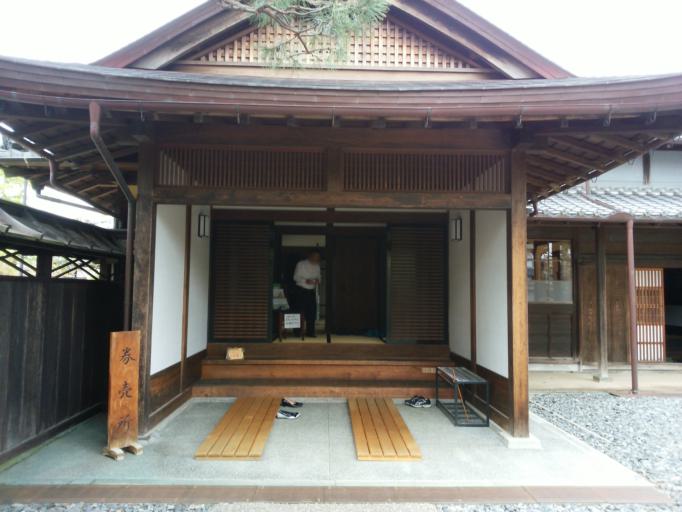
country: JP
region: Shizuoka
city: Kakegawa
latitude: 34.7766
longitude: 138.0147
